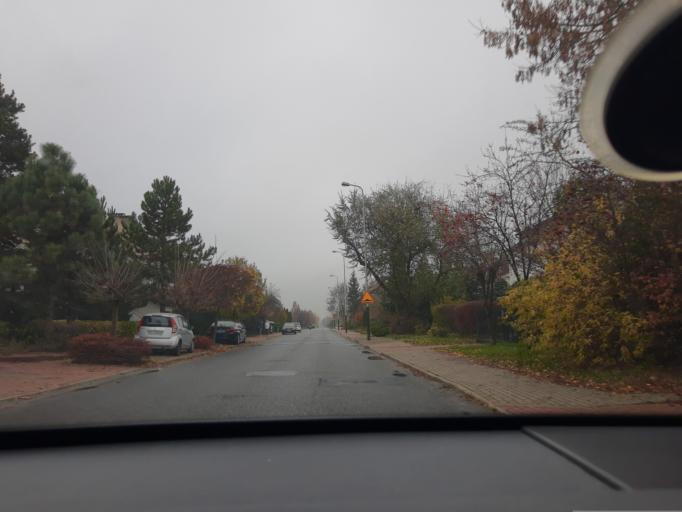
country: PL
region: Lodz Voivodeship
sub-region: Powiat pabianicki
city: Konstantynow Lodzki
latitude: 51.7403
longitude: 19.3792
